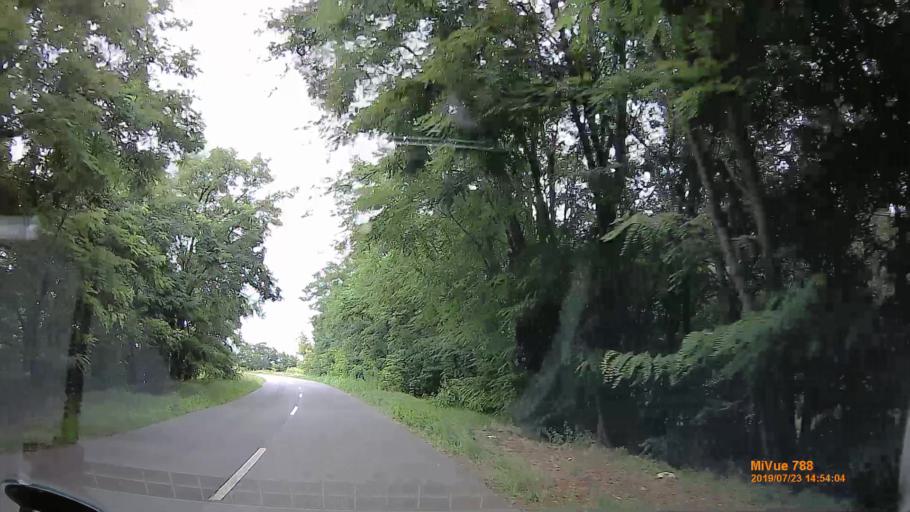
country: HU
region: Szabolcs-Szatmar-Bereg
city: Kalmanhaza
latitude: 47.8829
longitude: 21.6525
